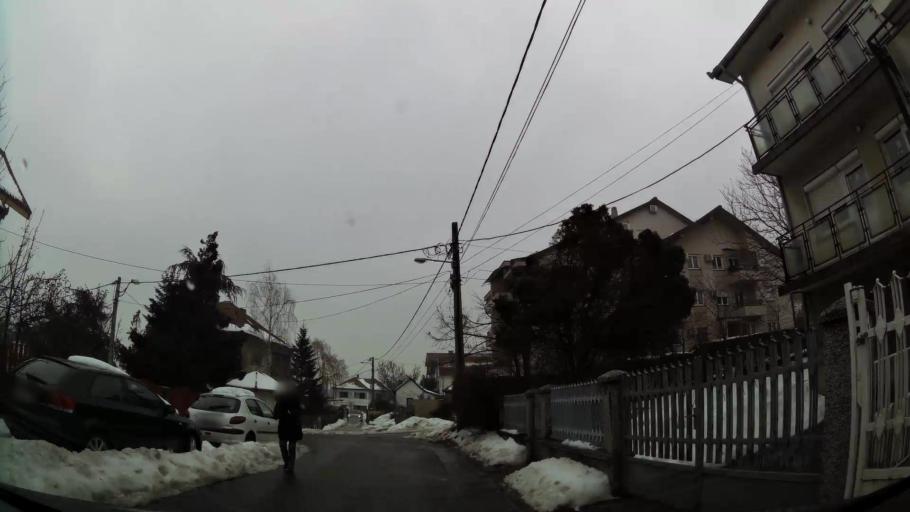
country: RS
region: Central Serbia
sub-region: Belgrade
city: Zvezdara
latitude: 44.7402
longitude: 20.5050
